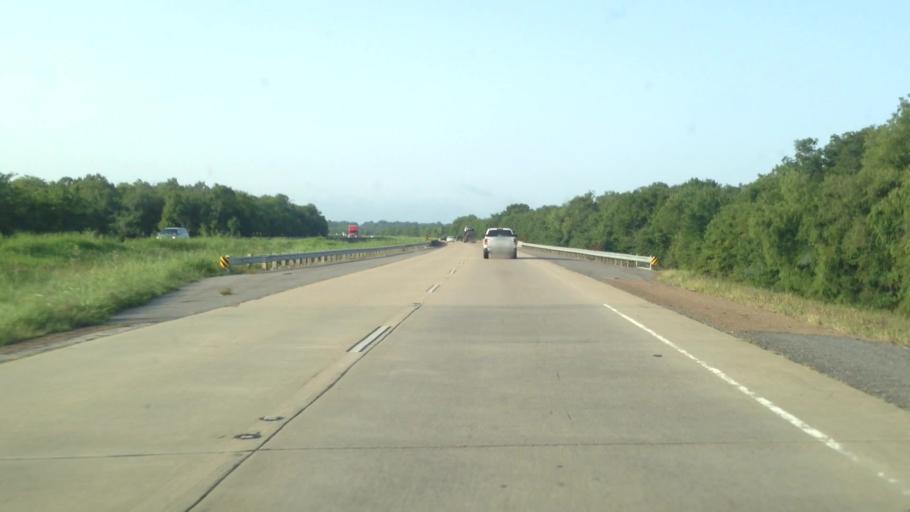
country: US
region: Louisiana
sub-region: Rapides Parish
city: Woodworth
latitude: 31.2003
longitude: -92.4743
